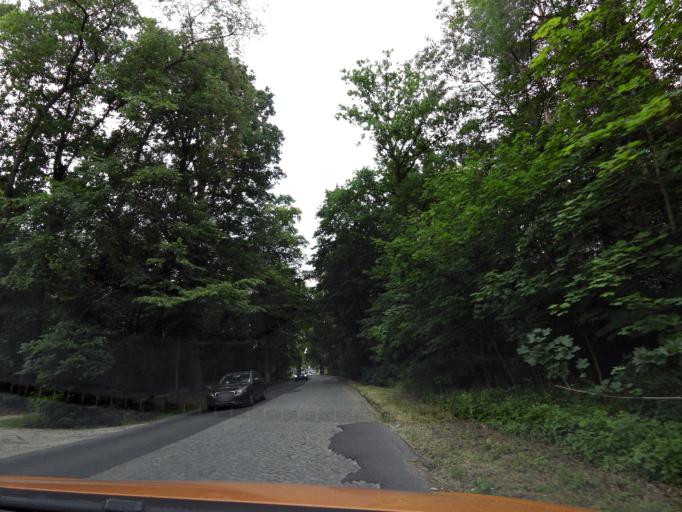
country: DE
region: Brandenburg
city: Rangsdorf
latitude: 52.3255
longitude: 13.3914
